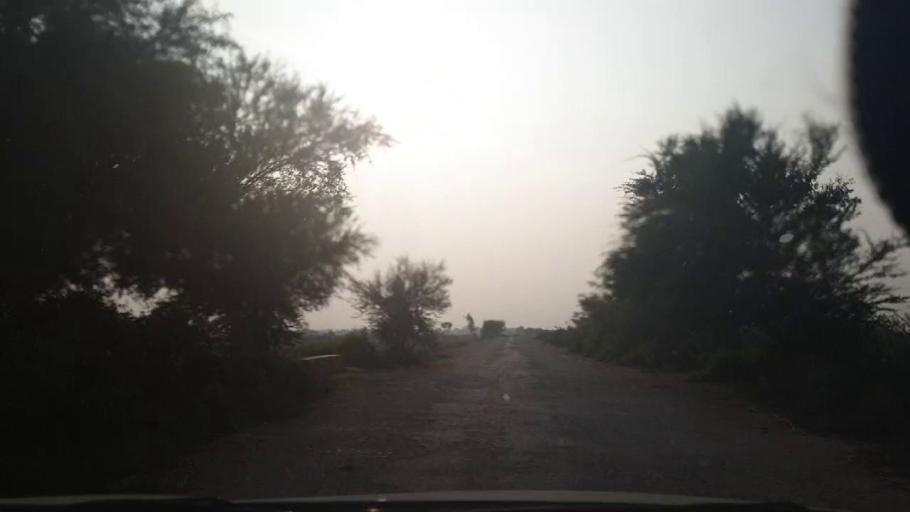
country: PK
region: Sindh
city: Bulri
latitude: 24.8508
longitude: 68.3488
